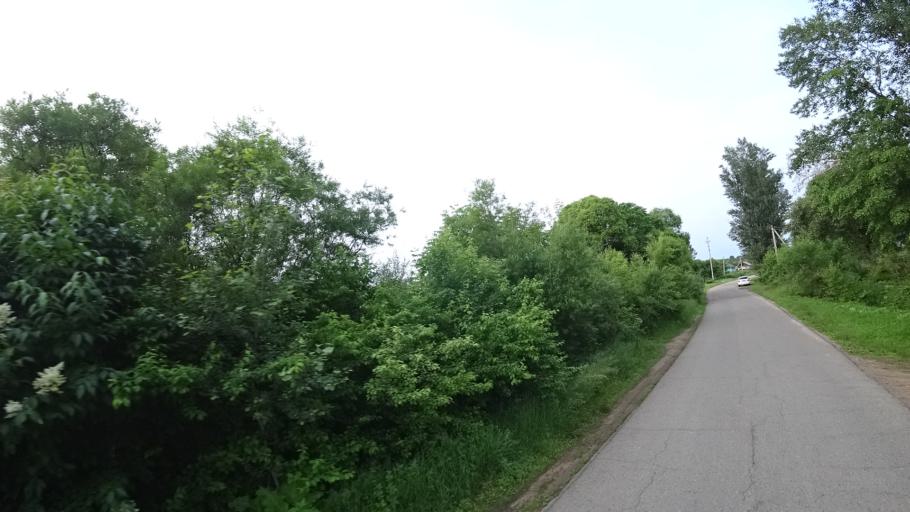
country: RU
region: Primorskiy
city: Novosysoyevka
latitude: 44.2458
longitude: 133.3710
